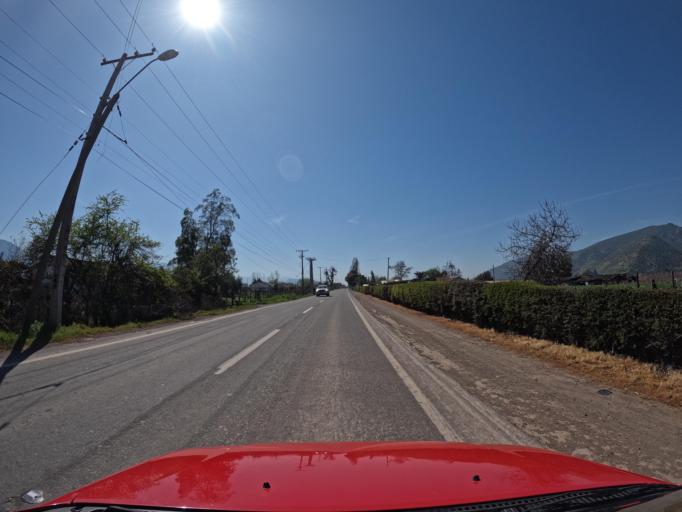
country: CL
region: Maule
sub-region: Provincia de Curico
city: Rauco
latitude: -35.0291
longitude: -71.4387
